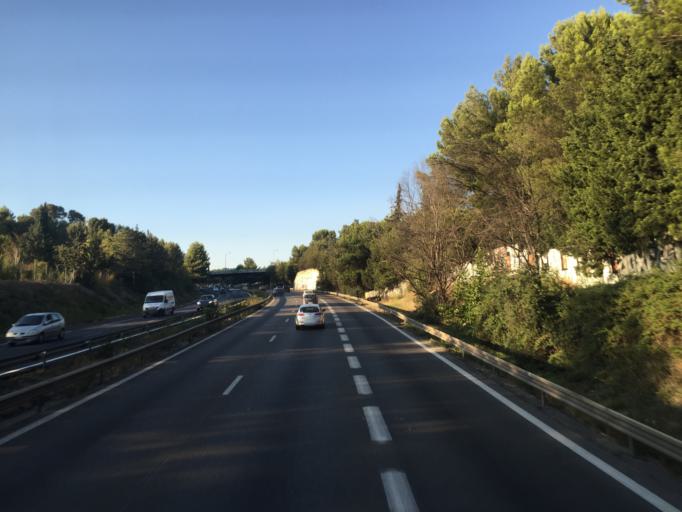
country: FR
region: Provence-Alpes-Cote d'Azur
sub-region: Departement des Bouches-du-Rhone
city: Aix-en-Provence
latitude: 43.5370
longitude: 5.4321
